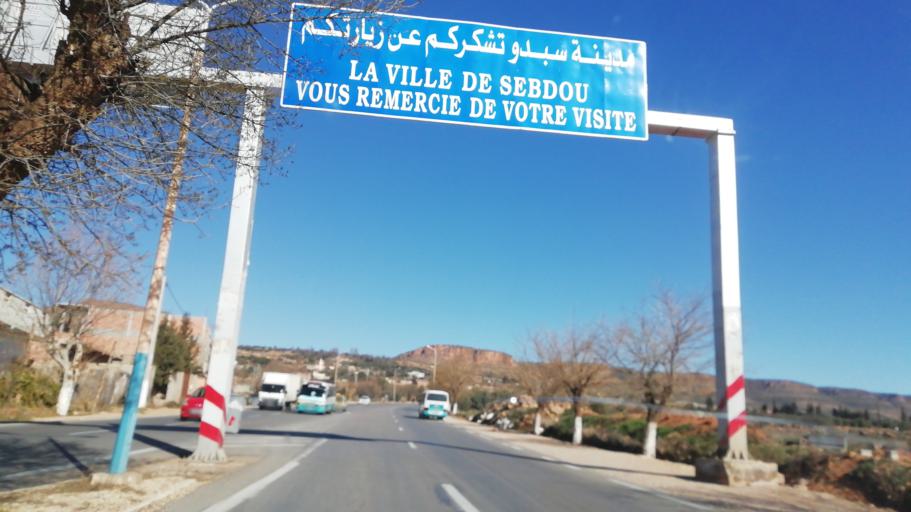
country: DZ
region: Tlemcen
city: Sebdou
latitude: 34.6717
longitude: -1.3183
